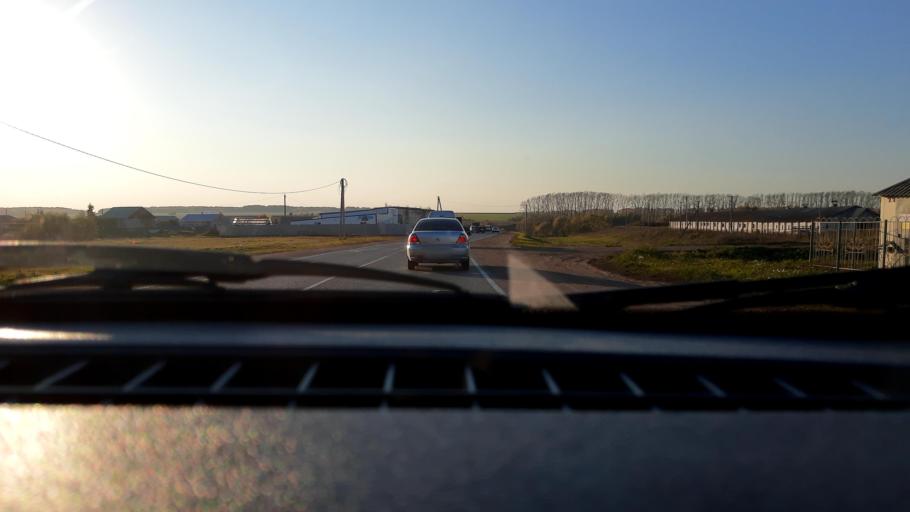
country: RU
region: Bashkortostan
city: Avdon
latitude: 54.8212
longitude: 55.6930
